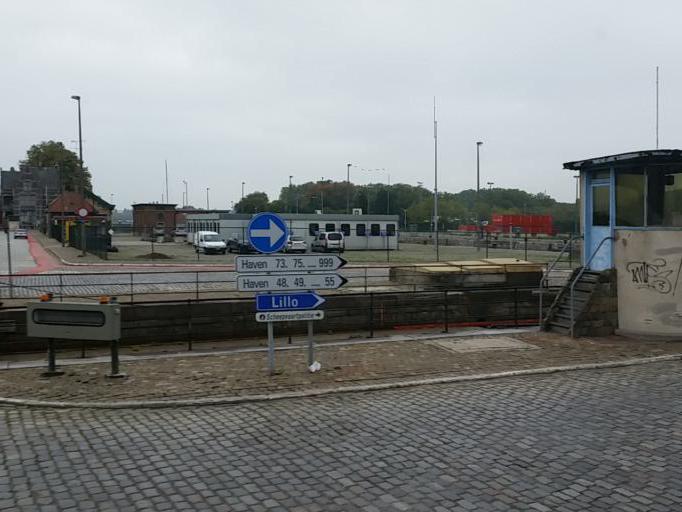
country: BE
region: Flanders
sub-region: Provincie Antwerpen
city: Antwerpen
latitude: 51.2415
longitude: 4.4045
